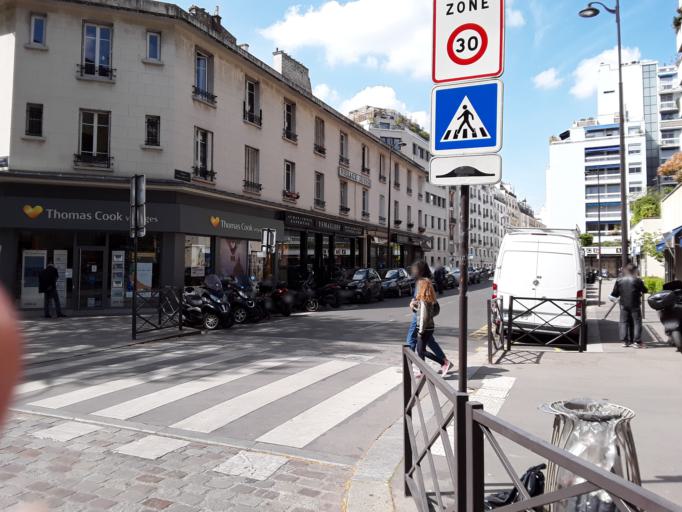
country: FR
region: Ile-de-France
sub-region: Departement des Hauts-de-Seine
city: Vanves
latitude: 48.8504
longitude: 2.2996
